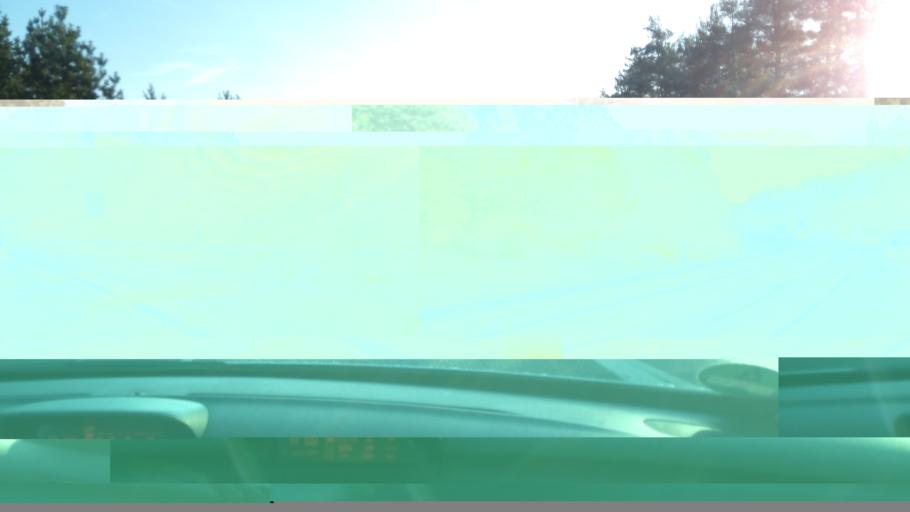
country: DE
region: Mecklenburg-Vorpommern
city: Neustrelitz
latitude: 53.3725
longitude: 13.0804
